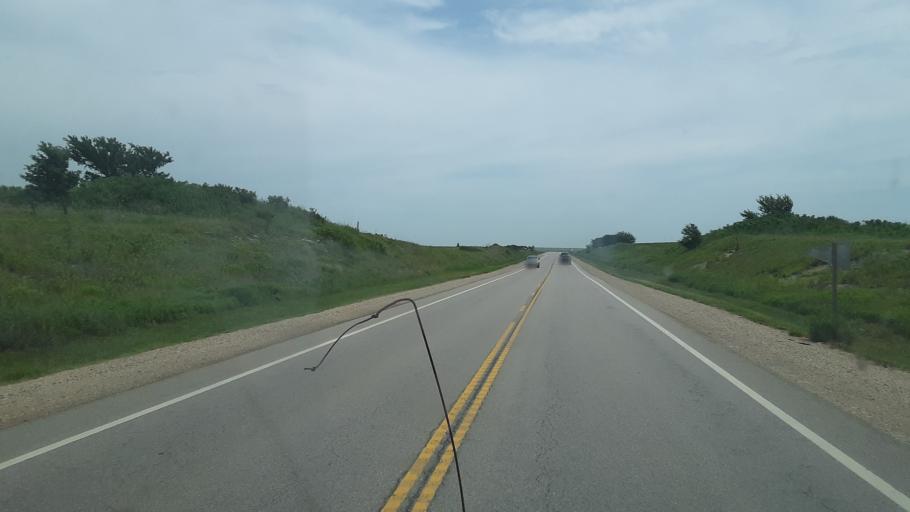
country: US
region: Kansas
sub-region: Greenwood County
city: Eureka
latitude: 37.8137
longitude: -96.4866
